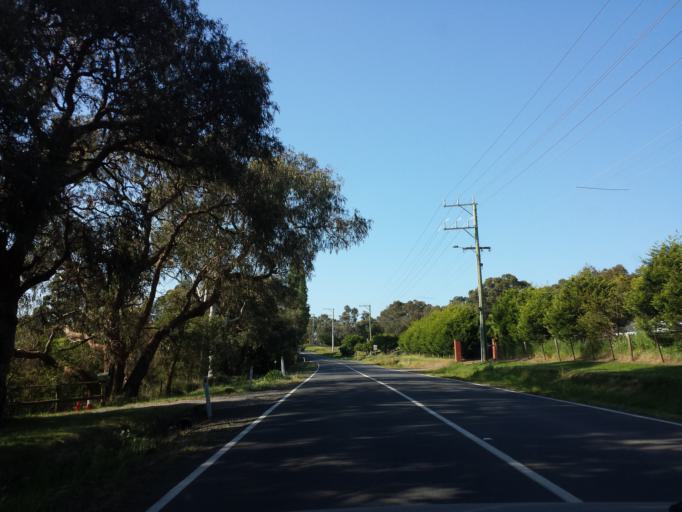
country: AU
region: Victoria
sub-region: Yarra Ranges
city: Belgrave South
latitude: -37.9438
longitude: 145.3550
